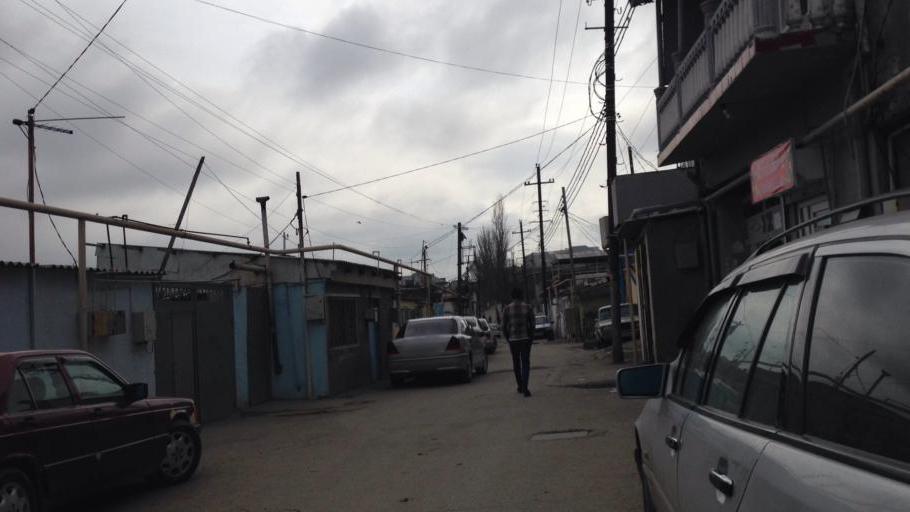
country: AZ
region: Baki
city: Bilajari
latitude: 40.4048
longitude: 49.8263
